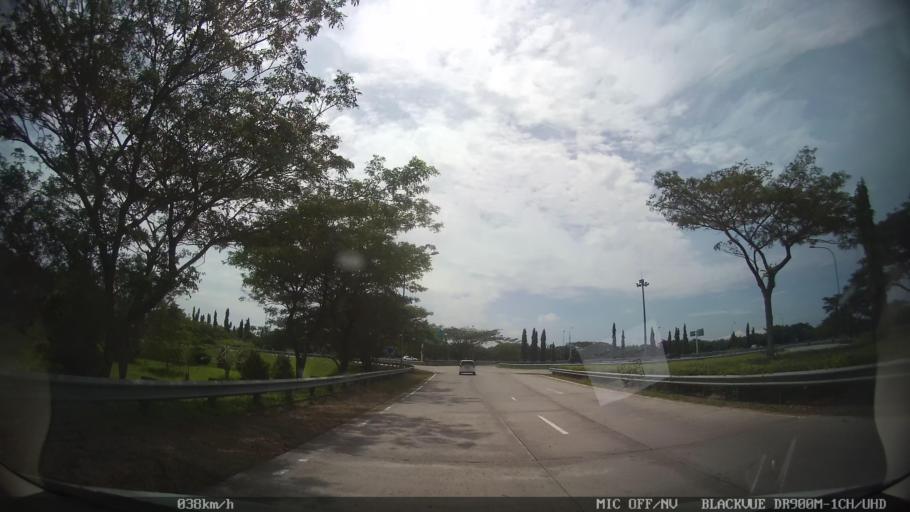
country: ID
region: North Sumatra
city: Percut
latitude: 3.6324
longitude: 98.8761
